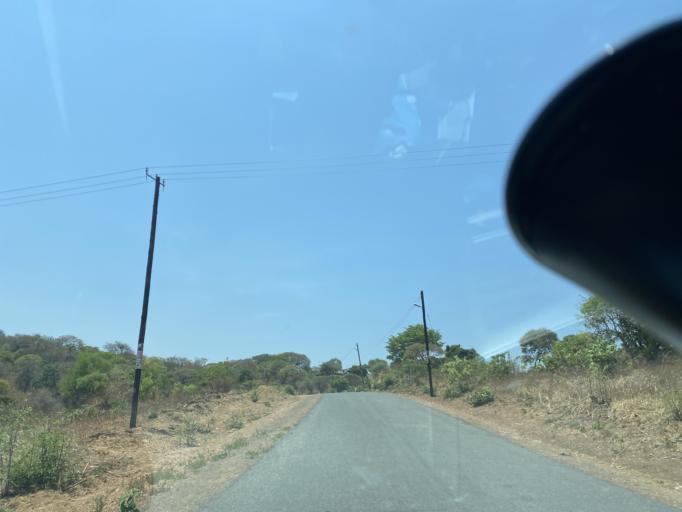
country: ZM
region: Lusaka
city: Kafue
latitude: -15.8678
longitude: 28.4357
